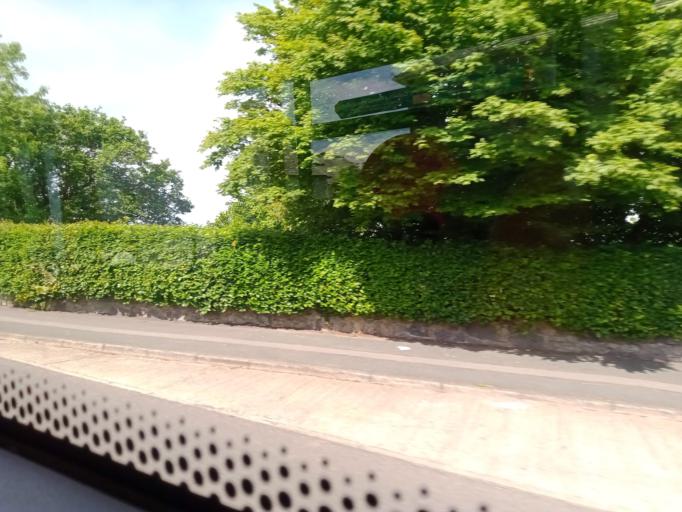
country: GB
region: Wales
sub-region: Anglesey
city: Menai Bridge
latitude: 53.2124
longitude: -4.1579
